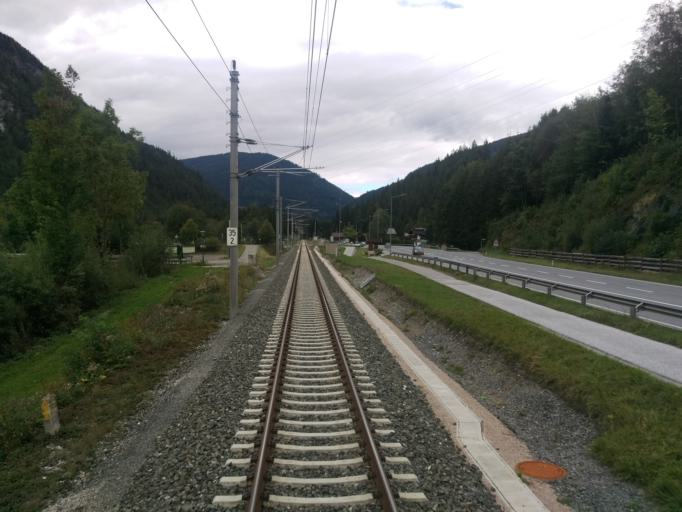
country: AT
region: Salzburg
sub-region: Politischer Bezirk Sankt Johann im Pongau
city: Forstau
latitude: 47.3898
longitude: 13.5975
